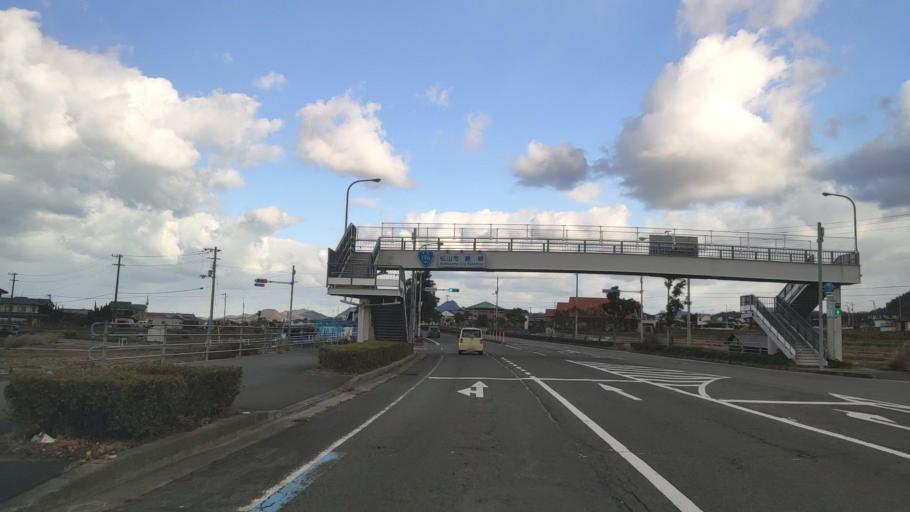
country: JP
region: Ehime
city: Hojo
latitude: 33.9376
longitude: 132.7731
